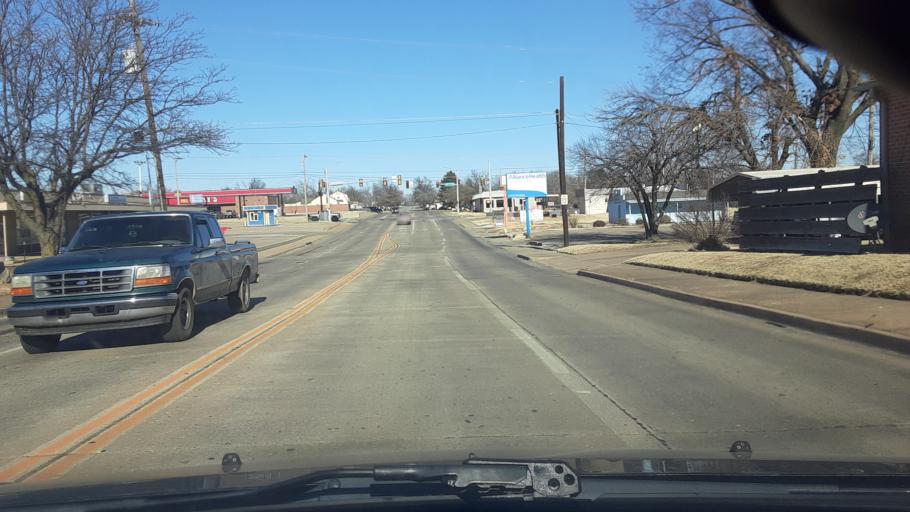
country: US
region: Oklahoma
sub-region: Kay County
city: Ponca City
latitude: 36.7229
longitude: -97.0787
